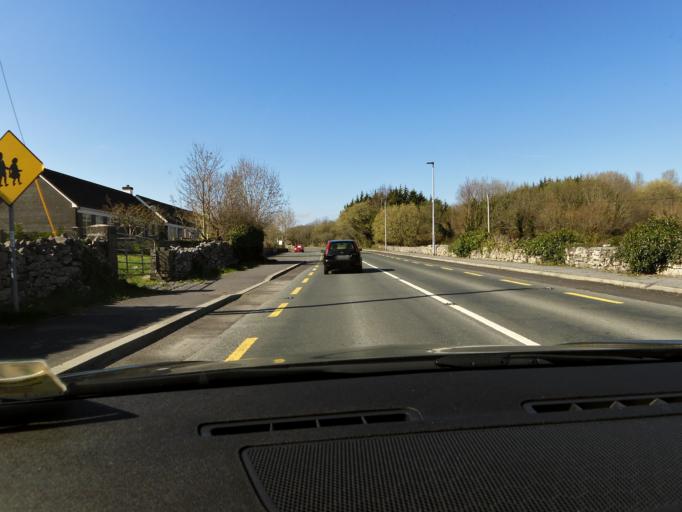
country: IE
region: Connaught
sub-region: County Galway
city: Moycullen
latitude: 53.3904
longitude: -9.2473
